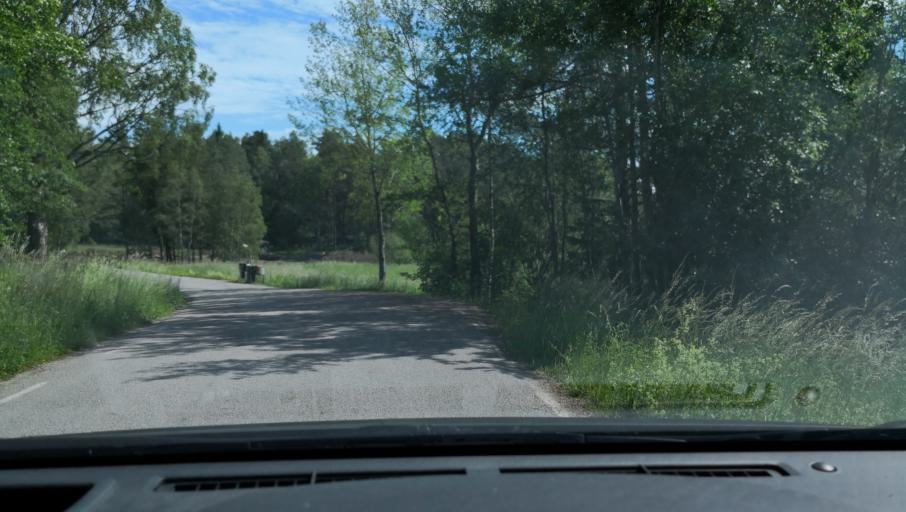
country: SE
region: Uppsala
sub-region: Uppsala Kommun
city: Alsike
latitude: 59.7040
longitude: 17.6851
